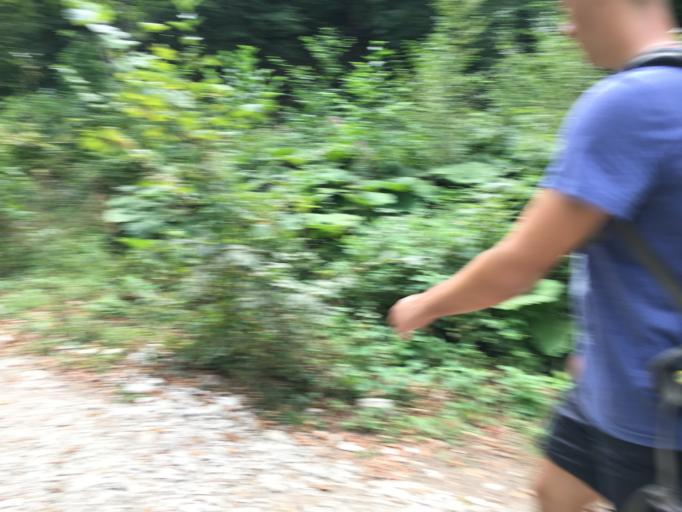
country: RU
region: Krasnodarskiy
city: Tuapse
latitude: 44.2639
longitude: 39.2137
